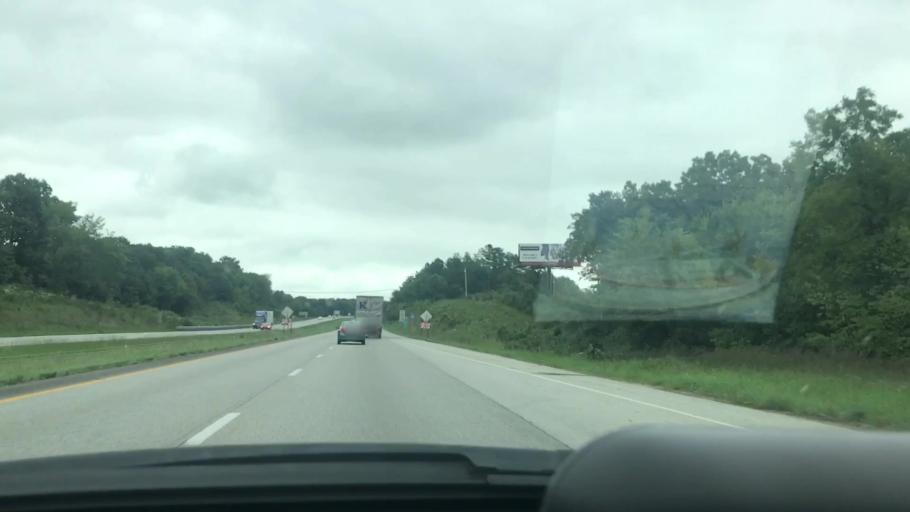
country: US
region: Missouri
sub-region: Jasper County
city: Joplin
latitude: 37.0391
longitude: -94.5104
